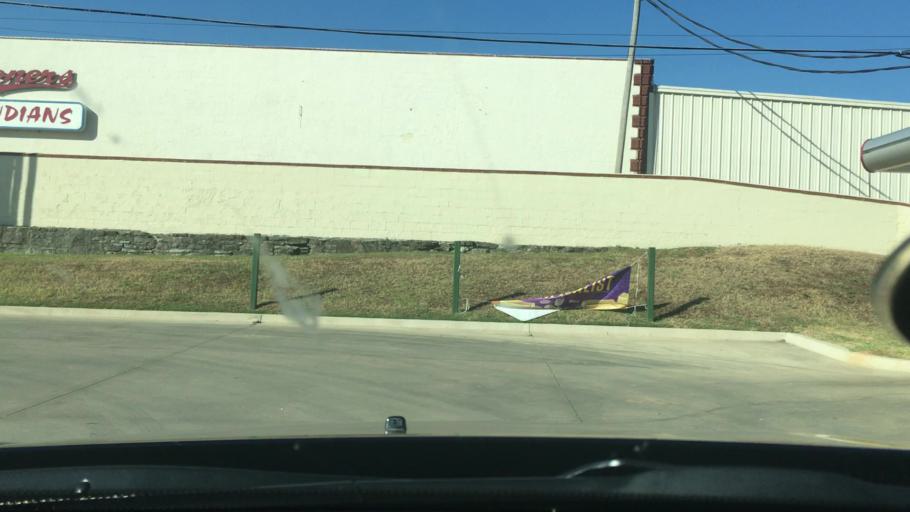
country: US
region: Oklahoma
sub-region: Johnston County
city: Tishomingo
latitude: 34.2325
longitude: -96.6742
